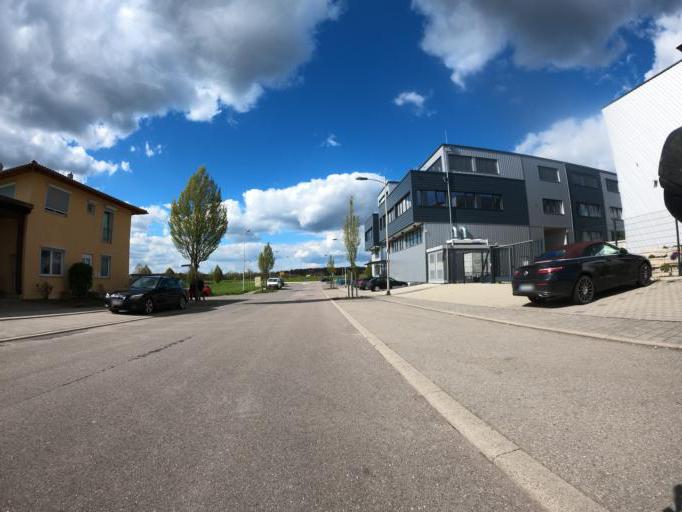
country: DE
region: Baden-Wuerttemberg
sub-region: Regierungsbezirk Stuttgart
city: Aidlingen
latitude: 48.7140
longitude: 8.9213
